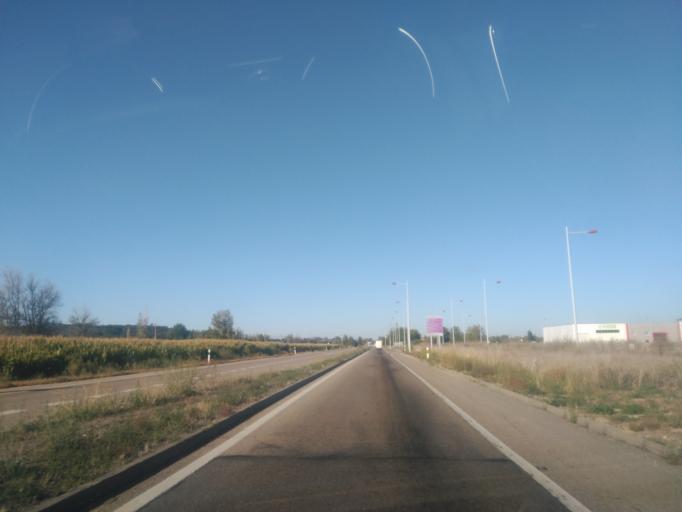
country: ES
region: Castille and Leon
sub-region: Provincia de Burgos
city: Villalba de Duero
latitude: 41.6640
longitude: -3.7330
